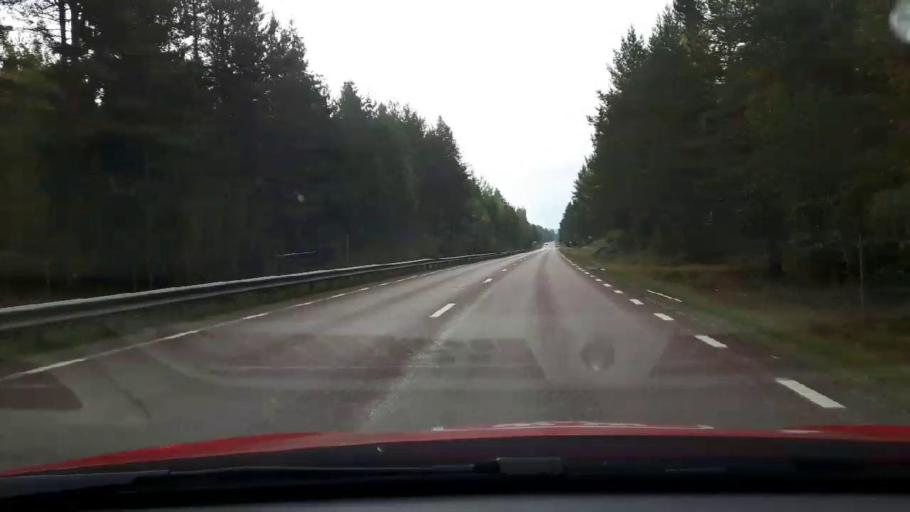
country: SE
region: Gaevleborg
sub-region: Bollnas Kommun
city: Kilafors
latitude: 61.2594
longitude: 16.5529
